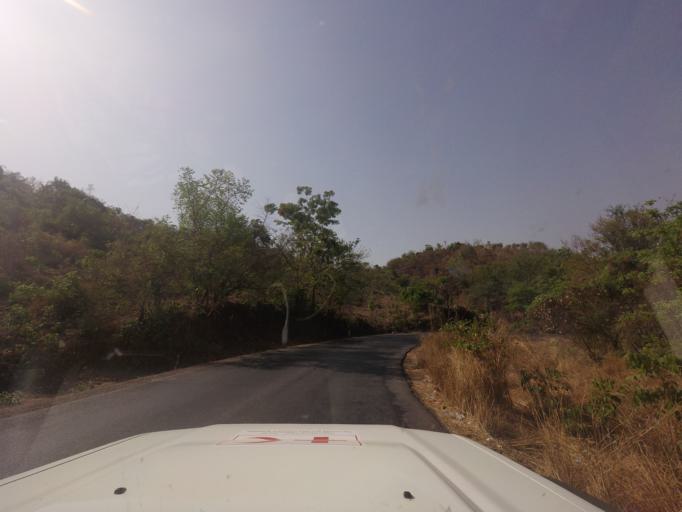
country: GN
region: Mamou
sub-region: Mamou Prefecture
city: Mamou
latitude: 10.2159
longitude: -12.4602
